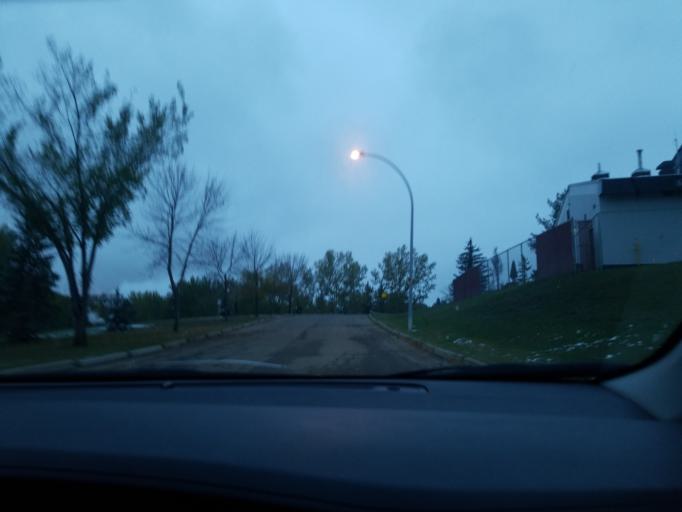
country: CA
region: Alberta
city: Edmonton
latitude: 53.5553
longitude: -113.3925
